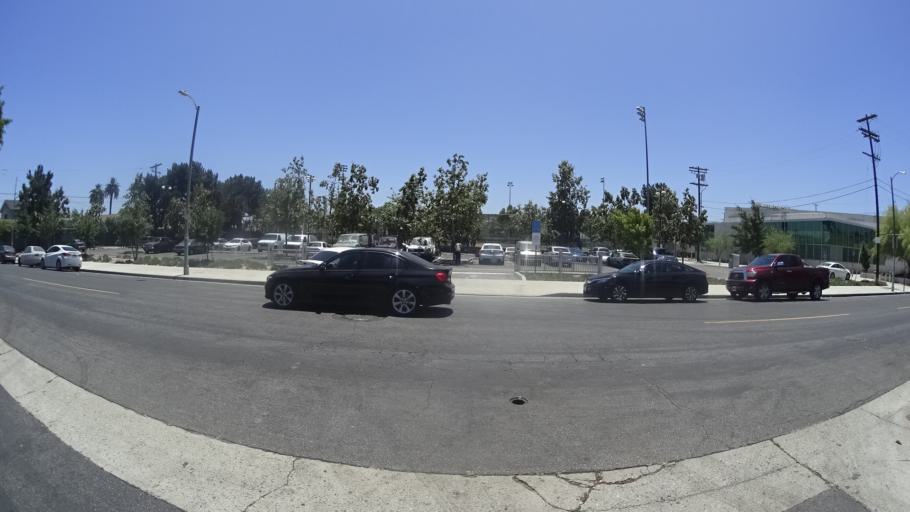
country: US
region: California
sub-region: Los Angeles County
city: View Park-Windsor Hills
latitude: 34.0148
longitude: -118.3077
